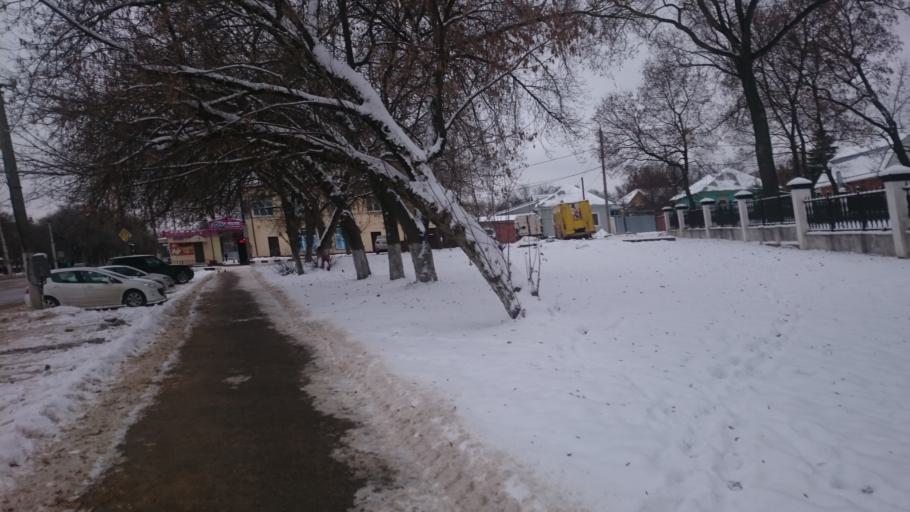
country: RU
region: Tula
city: Tula
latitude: 54.1782
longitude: 37.6277
